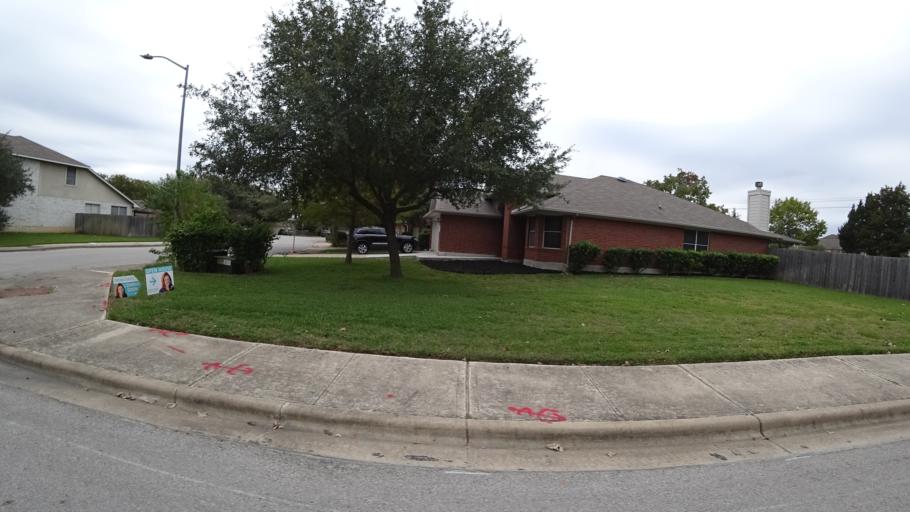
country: US
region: Texas
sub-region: Travis County
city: Shady Hollow
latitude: 30.1509
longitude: -97.8553
